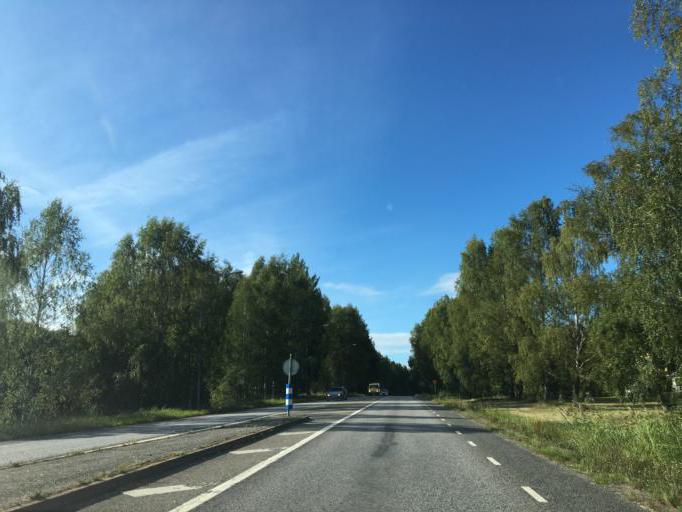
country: SE
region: Soedermanland
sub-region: Nykopings Kommun
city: Nykoping
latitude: 58.7772
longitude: 16.9746
